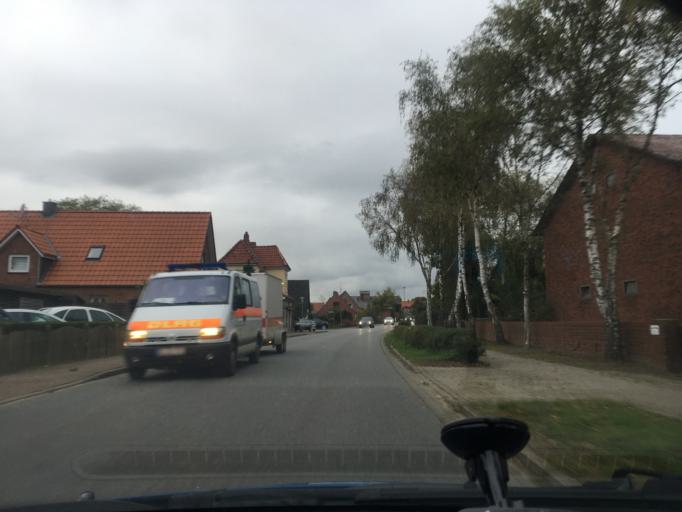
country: DE
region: Lower Saxony
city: Marschacht
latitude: 53.4121
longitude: 10.3834
